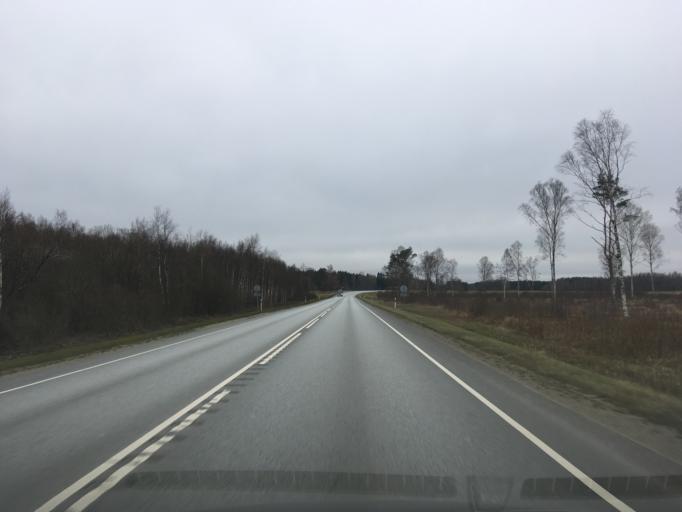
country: EE
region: Laeaene-Virumaa
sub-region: Viru-Nigula vald
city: Kunda
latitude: 59.4165
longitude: 26.6537
